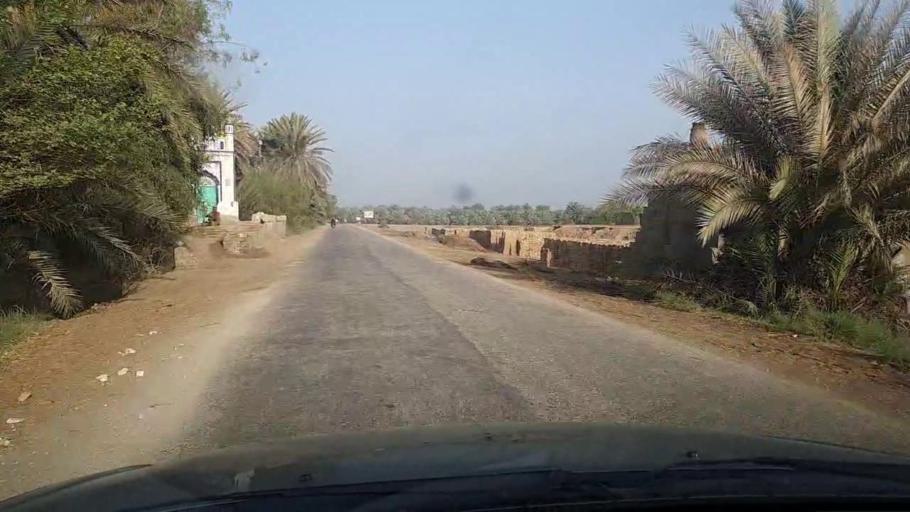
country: PK
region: Sindh
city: Pir jo Goth
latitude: 27.5547
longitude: 68.6819
